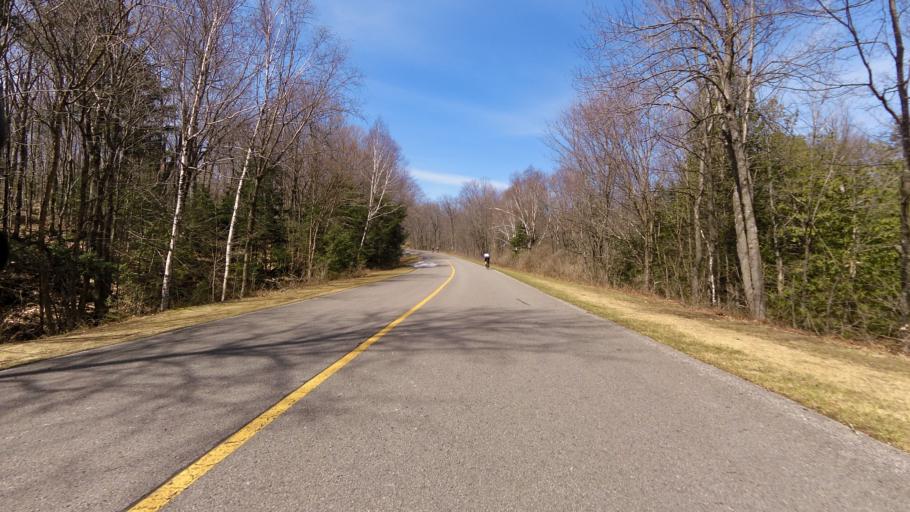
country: CA
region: Quebec
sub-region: Outaouais
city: Gatineau
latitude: 45.4805
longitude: -75.8492
